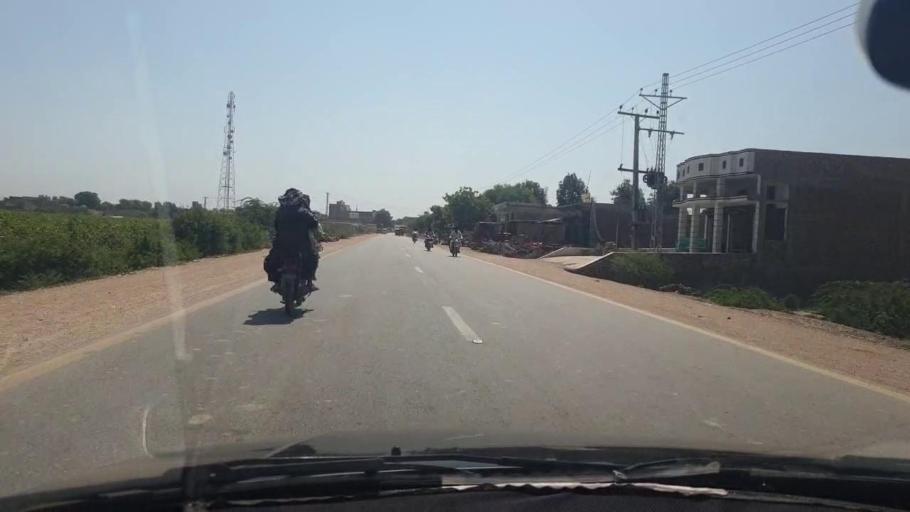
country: PK
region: Sindh
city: Chambar
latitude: 25.3024
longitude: 68.8097
